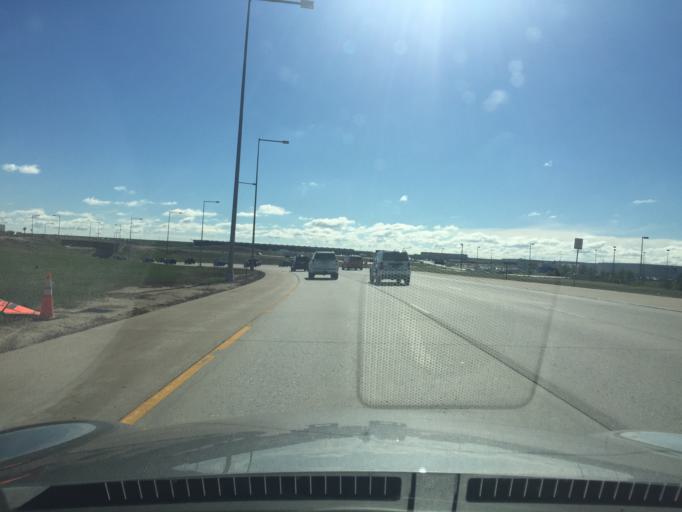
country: US
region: Colorado
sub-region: Weld County
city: Lochbuie
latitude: 39.8335
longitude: -104.6765
